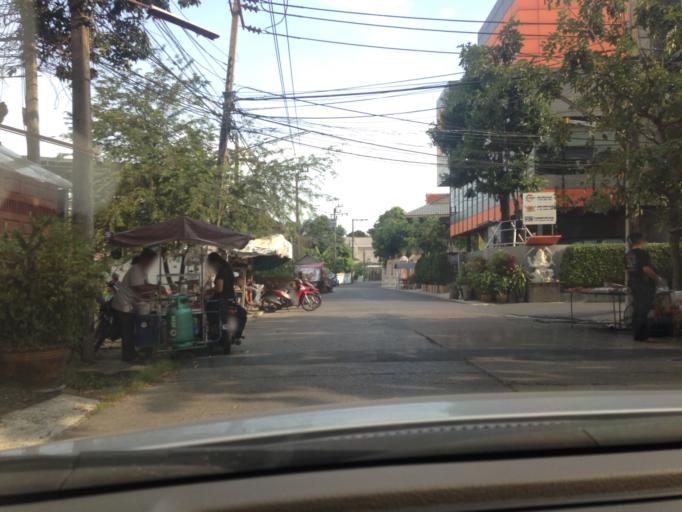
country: TH
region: Bangkok
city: Khan Na Yao
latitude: 13.8377
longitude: 100.6441
